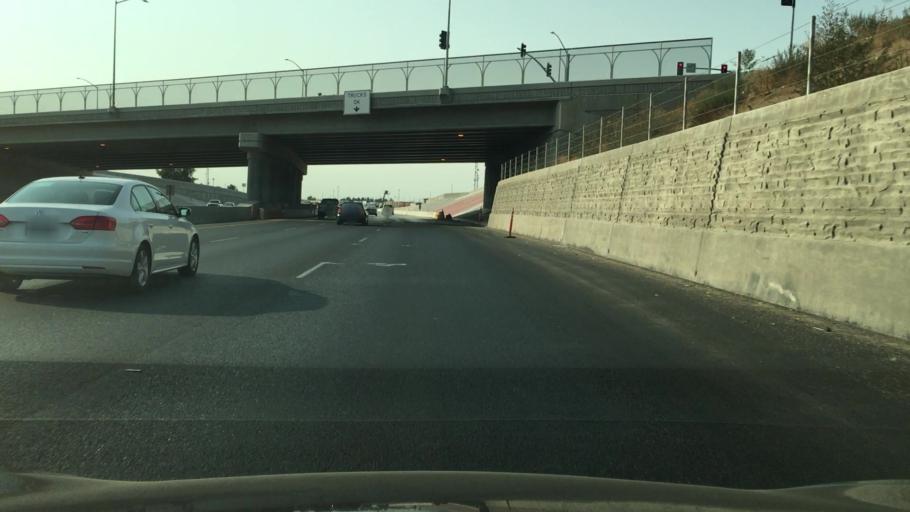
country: US
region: California
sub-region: Fresno County
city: West Park
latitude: 36.7713
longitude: -119.8381
